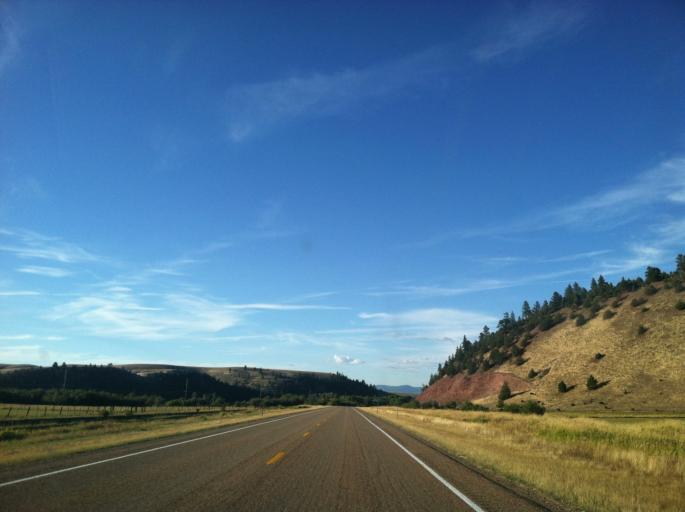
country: US
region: Montana
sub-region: Granite County
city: Philipsburg
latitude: 46.5102
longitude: -113.2264
